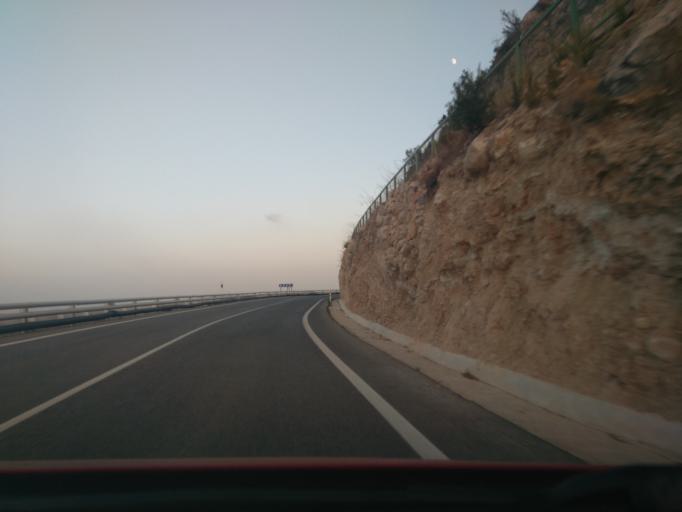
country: ES
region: Valencia
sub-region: Provincia de Valencia
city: Sumacarcer
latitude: 39.0906
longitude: -0.6269
